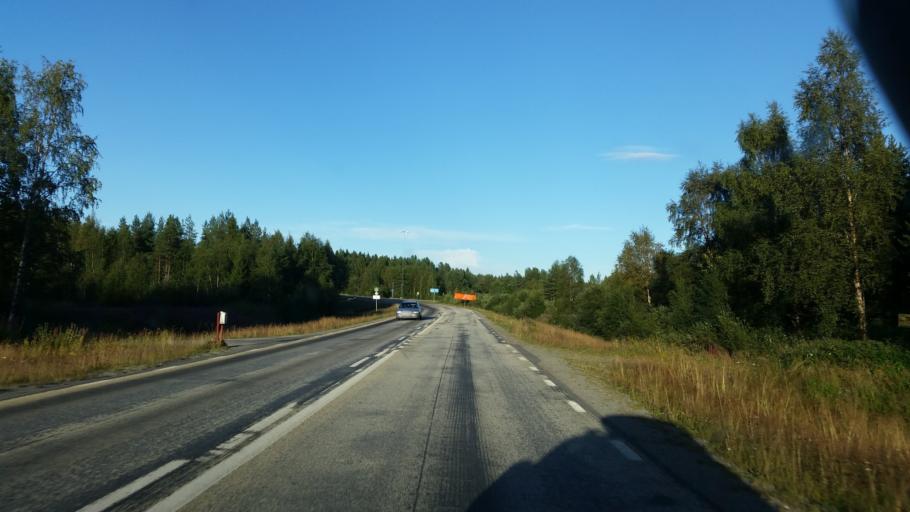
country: SE
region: Vaesterbotten
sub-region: Dorotea Kommun
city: Dorotea
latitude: 64.2532
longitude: 16.4730
